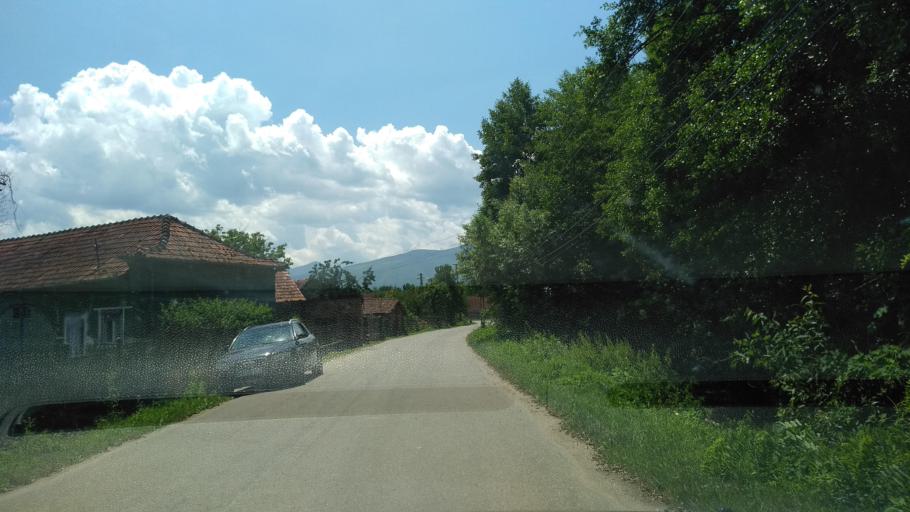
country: RO
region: Hunedoara
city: Densus
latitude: 45.5531
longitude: 22.8229
